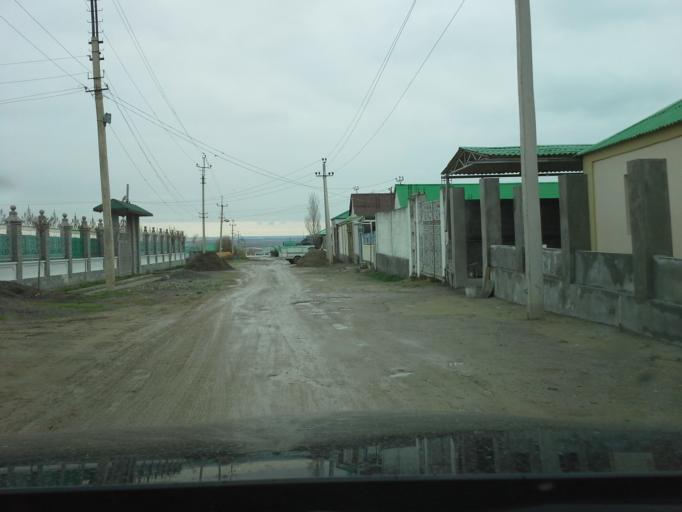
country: TM
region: Ahal
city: Abadan
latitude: 37.9571
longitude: 58.2006
